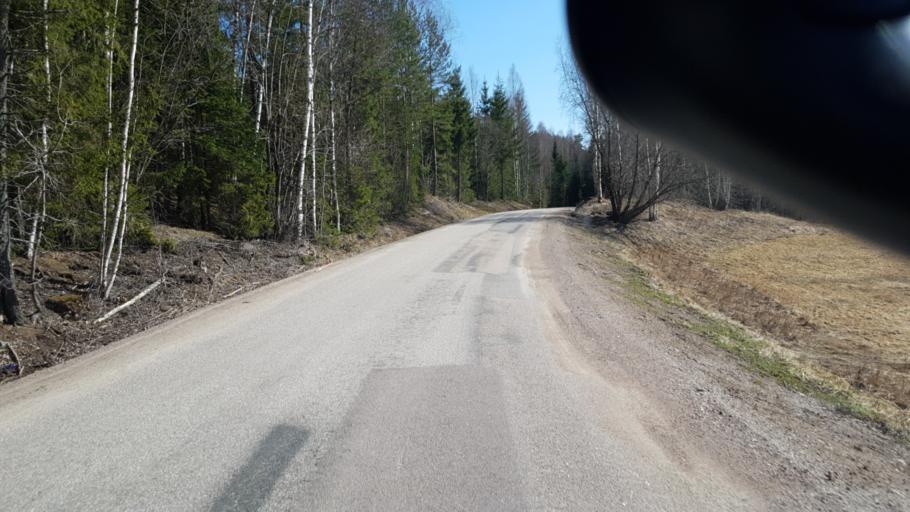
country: SE
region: Vaermland
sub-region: Arvika Kommun
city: Arvika
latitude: 59.6395
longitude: 12.8160
